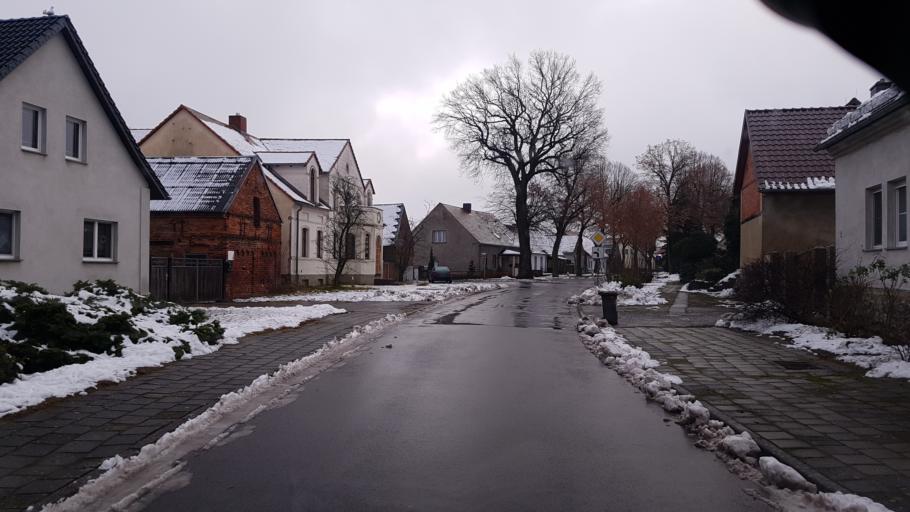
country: DE
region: Brandenburg
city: Neu Zauche
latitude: 51.9617
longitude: 14.1341
